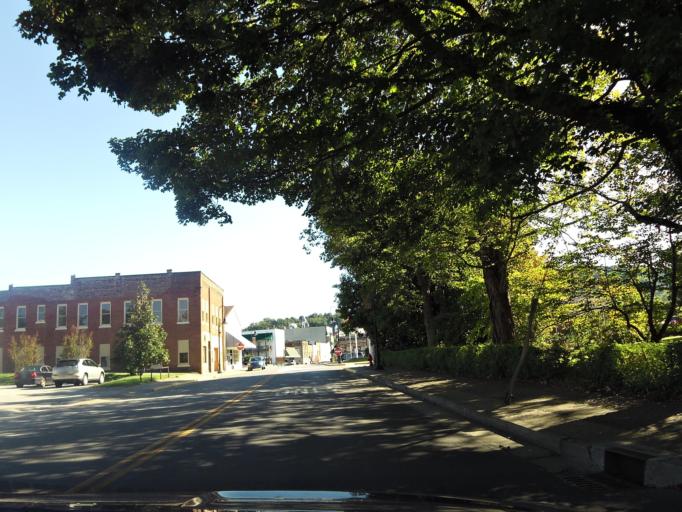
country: US
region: Kentucky
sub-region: Whitley County
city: Williamsburg
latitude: 36.7413
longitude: -84.1617
